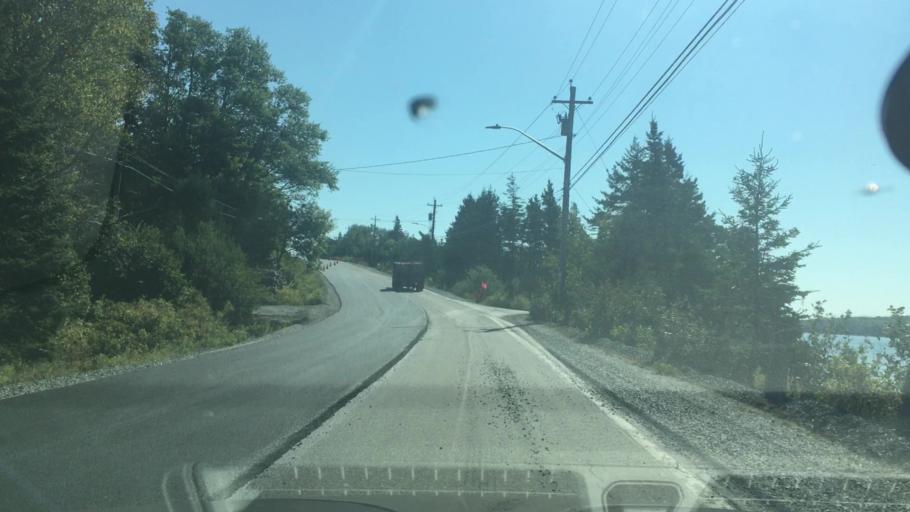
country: CA
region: Nova Scotia
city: New Glasgow
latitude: 44.9109
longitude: -62.5059
